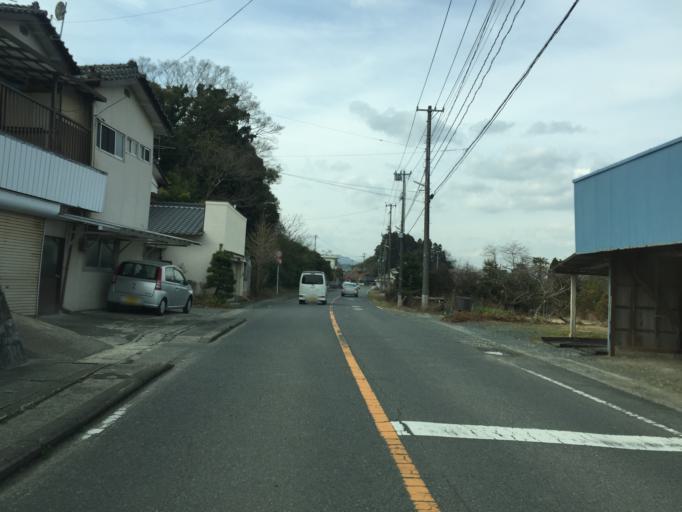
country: JP
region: Ibaraki
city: Kitaibaraki
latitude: 36.8864
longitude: 140.7831
